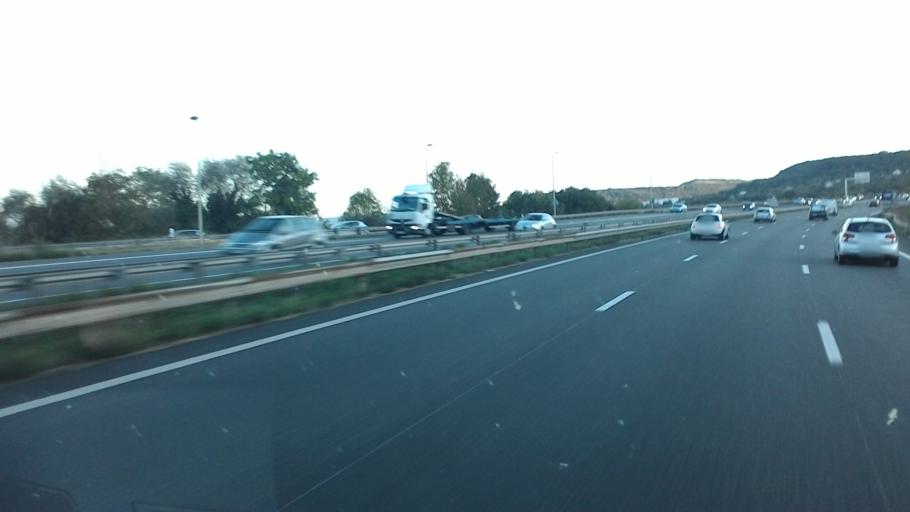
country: FR
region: Lorraine
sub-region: Departement de Meurthe-et-Moselle
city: Bouxieres-aux-Dames
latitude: 48.7511
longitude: 6.1569
